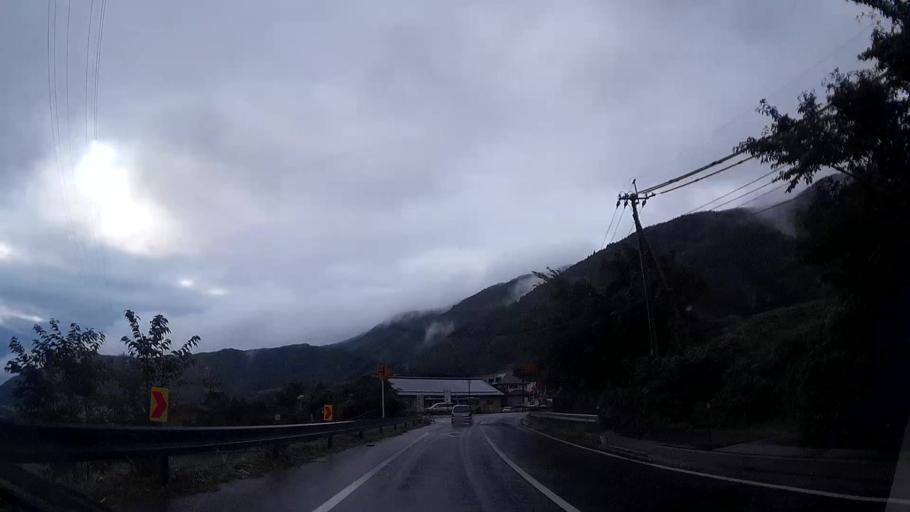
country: JP
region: Kumamoto
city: Ozu
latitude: 32.8768
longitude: 130.9761
